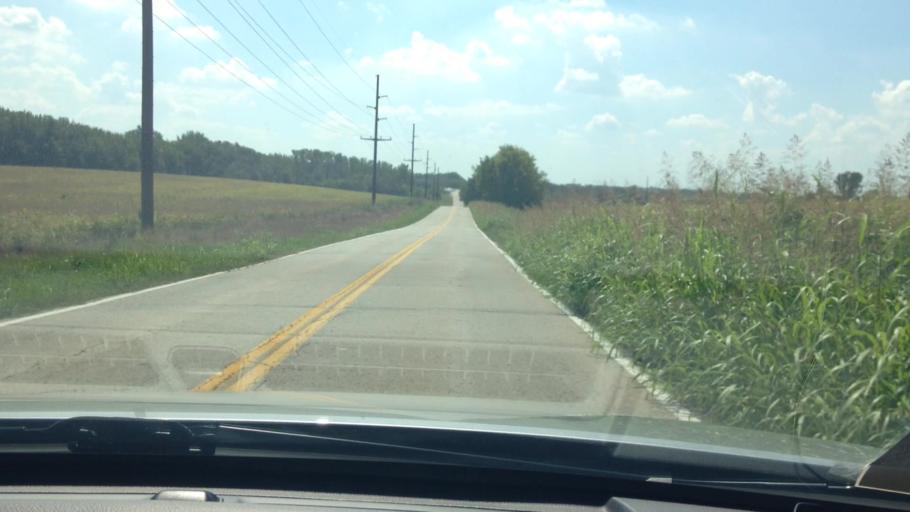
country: US
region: Missouri
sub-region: Platte County
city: Platte City
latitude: 39.3464
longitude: -94.7330
